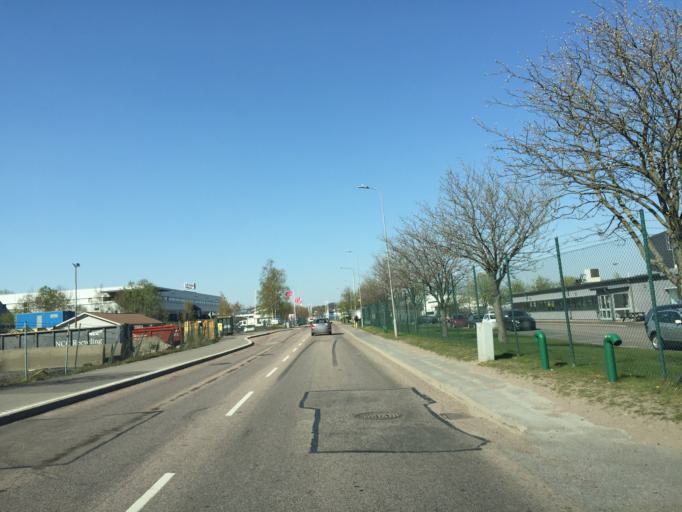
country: SE
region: Vaestra Goetaland
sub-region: Goteborg
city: Hammarkullen
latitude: 57.7813
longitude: 11.9943
